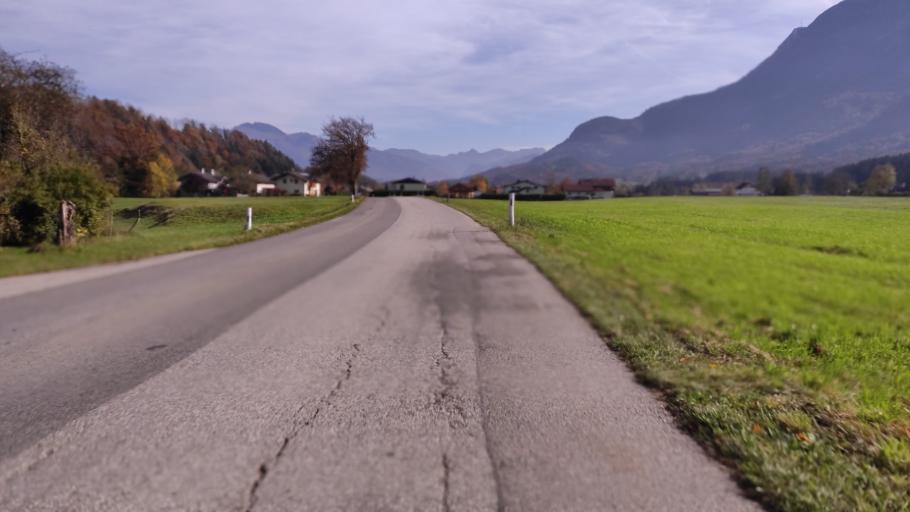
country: AT
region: Salzburg
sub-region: Politischer Bezirk Salzburg-Umgebung
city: Strobl
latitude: 47.7160
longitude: 13.5292
